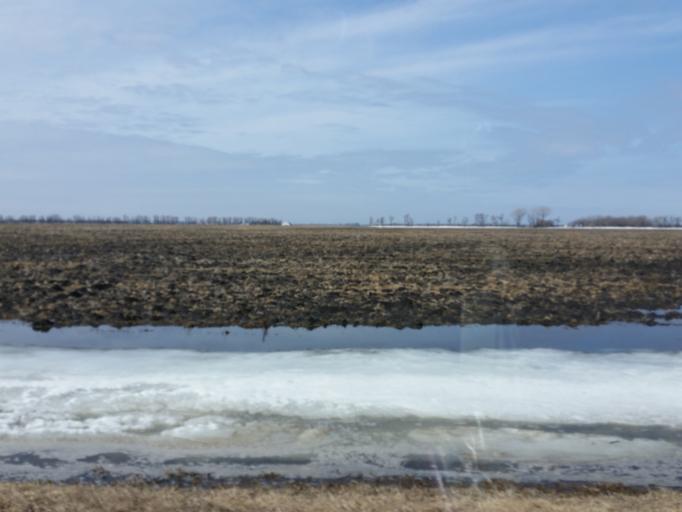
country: US
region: North Dakota
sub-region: Walsh County
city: Grafton
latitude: 48.3398
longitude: -97.2111
